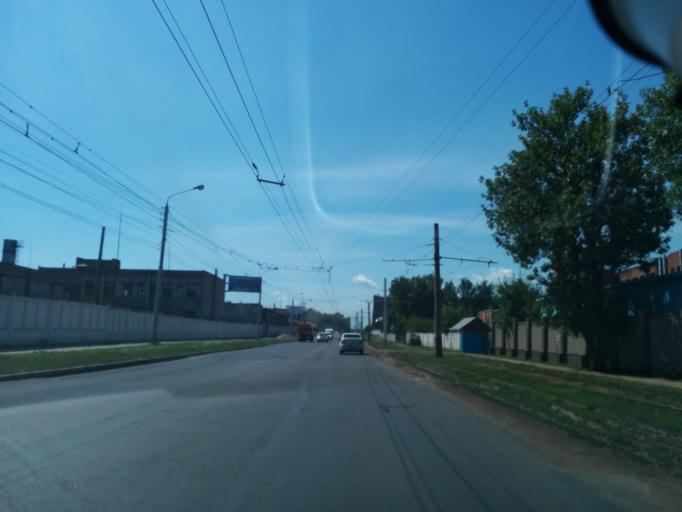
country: RU
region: Bashkortostan
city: Ufa
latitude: 54.7446
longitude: 55.9766
